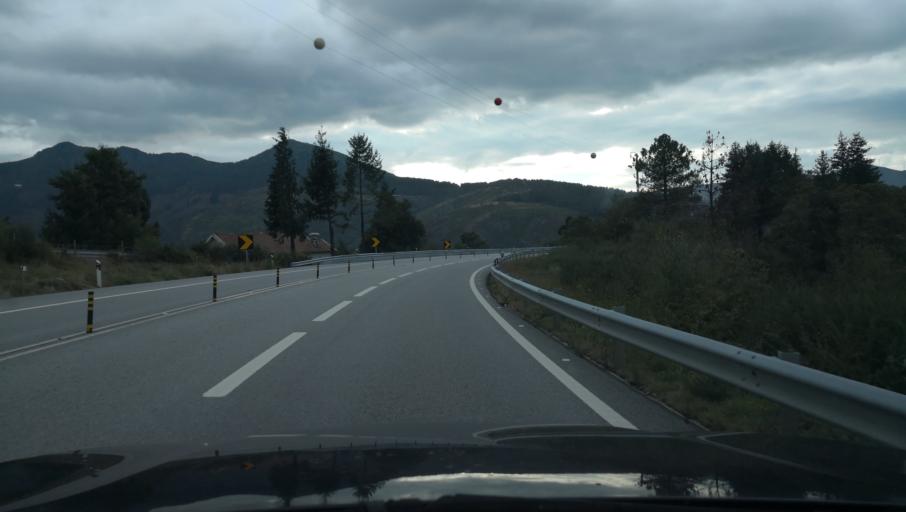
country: PT
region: Vila Real
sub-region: Santa Marta de Penaguiao
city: Santa Marta de Penaguiao
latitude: 41.2782
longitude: -7.8570
